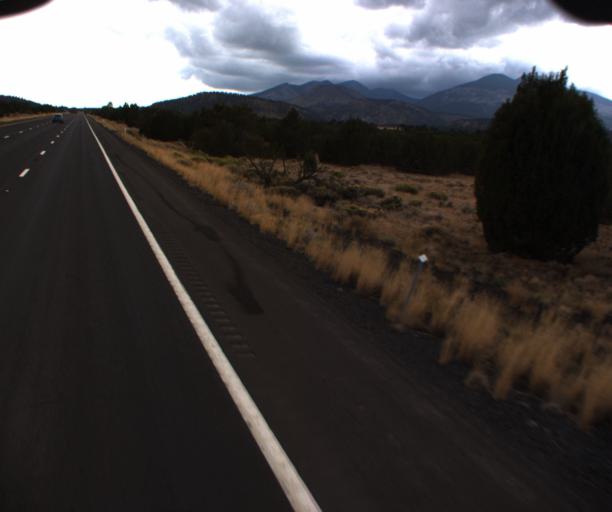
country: US
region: Arizona
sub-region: Coconino County
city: Flagstaff
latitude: 35.4113
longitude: -111.5735
